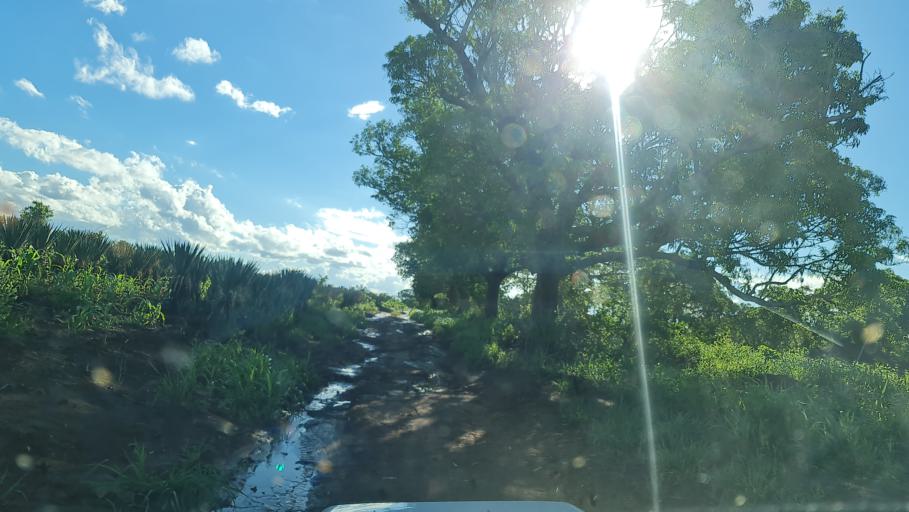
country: MZ
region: Nampula
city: Ilha de Mocambique
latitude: -14.9349
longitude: 40.2092
